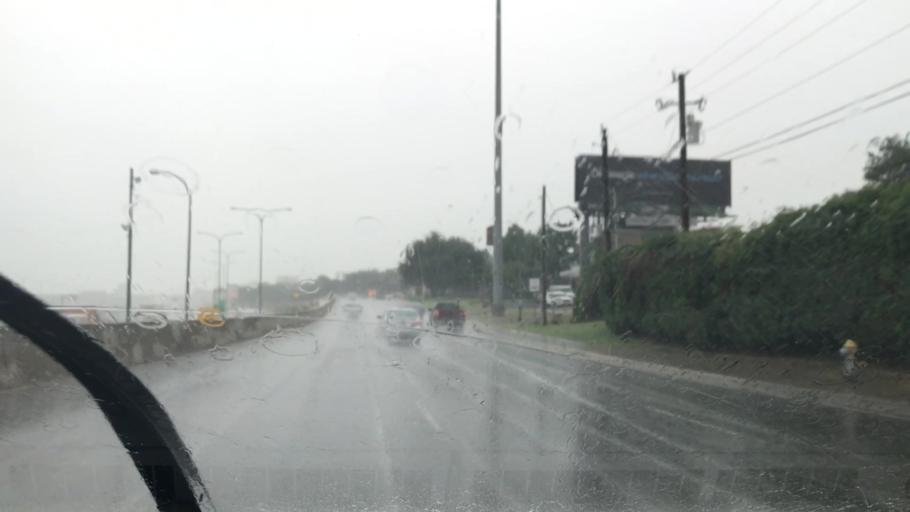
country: US
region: Texas
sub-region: Dallas County
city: Addison
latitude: 32.9246
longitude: -96.8024
